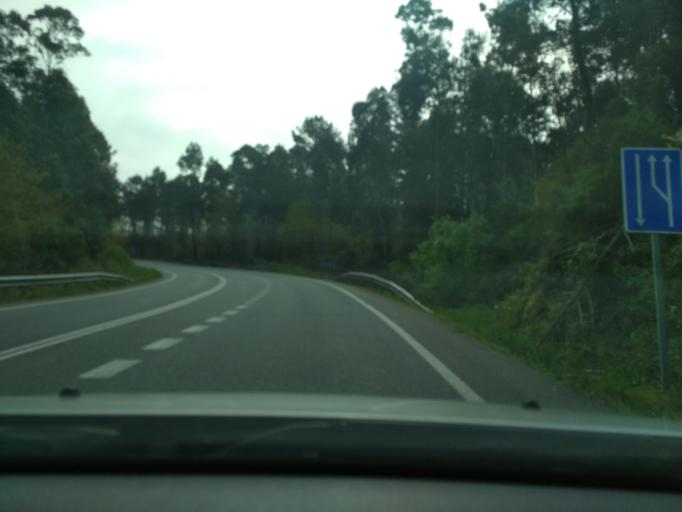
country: ES
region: Galicia
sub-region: Provincia de Pontevedra
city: Catoira
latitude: 42.6527
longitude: -8.6949
